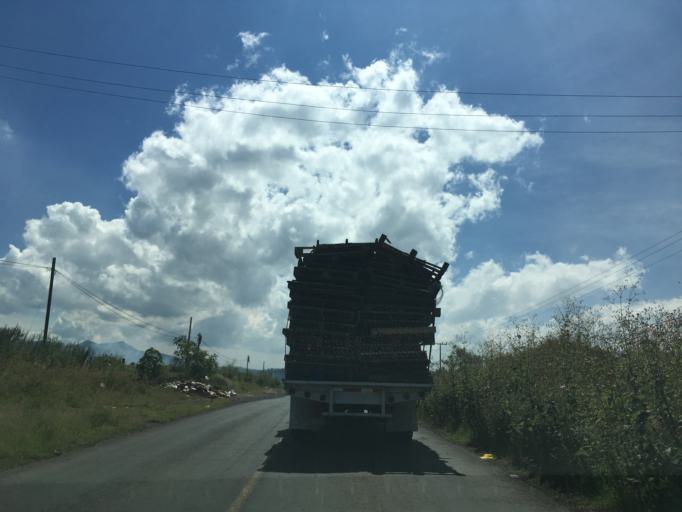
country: MX
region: Michoacan
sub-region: Morelia
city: La Mintzita (Piedra Dura)
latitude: 19.6651
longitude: -101.2834
